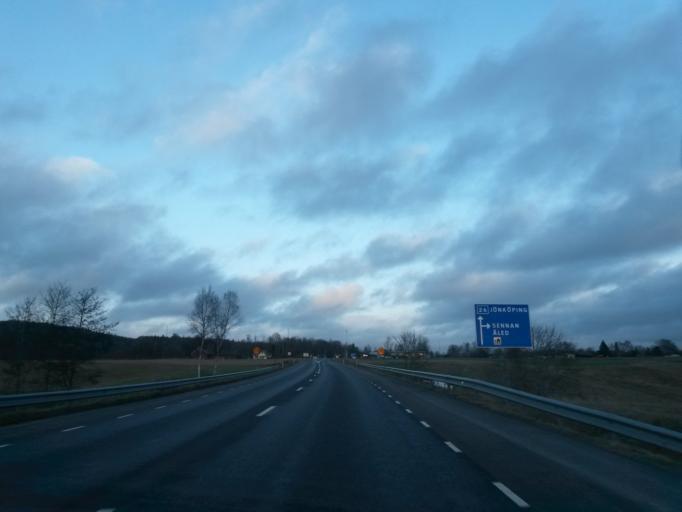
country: SE
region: Halland
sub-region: Halmstads Kommun
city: Aled
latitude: 56.7430
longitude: 12.9280
